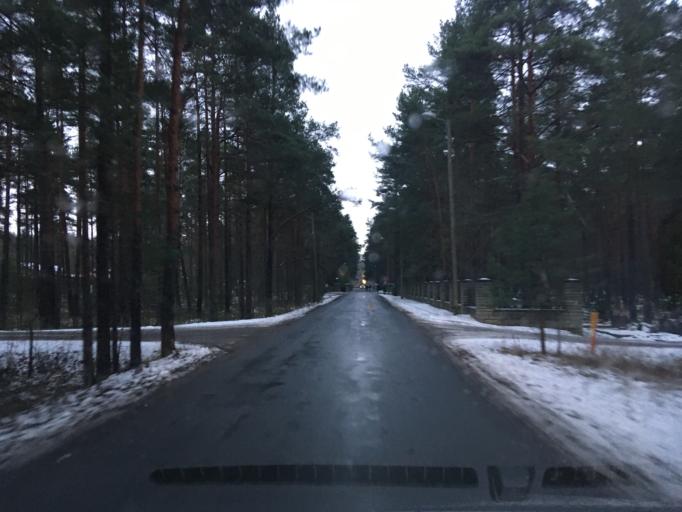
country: EE
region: Harju
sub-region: Tallinna linn
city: Tallinn
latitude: 59.3817
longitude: 24.7286
